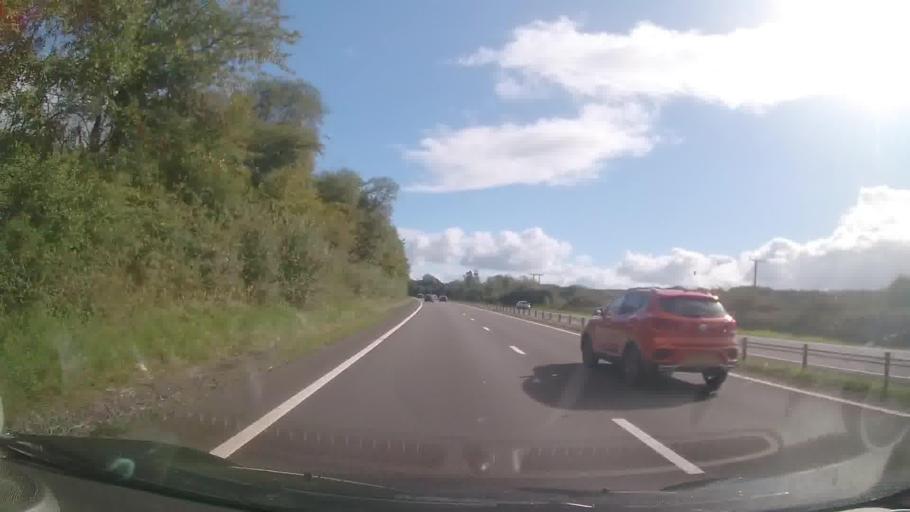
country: GB
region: Wales
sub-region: Carmarthenshire
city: Carmarthen
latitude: 51.8398
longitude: -4.2789
